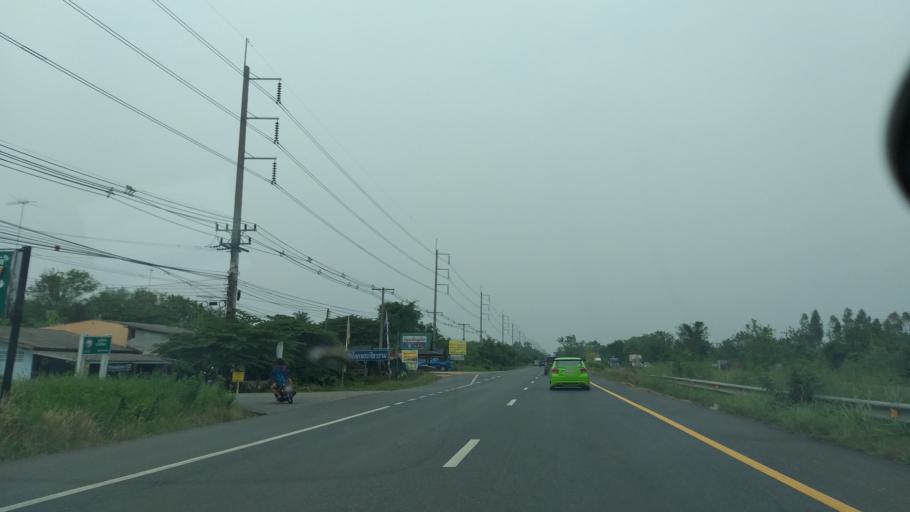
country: TH
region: Chon Buri
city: Ko Chan
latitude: 13.4066
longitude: 101.2819
